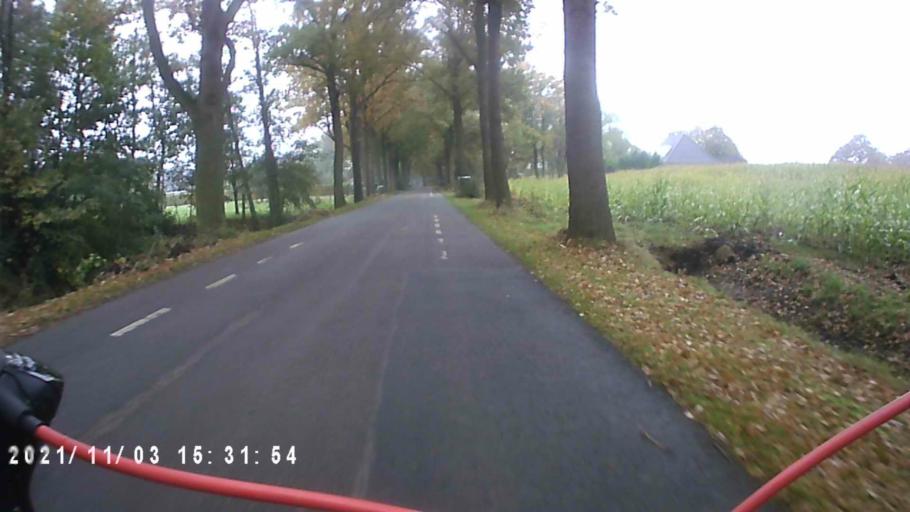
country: NL
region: Groningen
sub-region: Gemeente Leek
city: Leek
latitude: 53.1281
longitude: 6.3680
